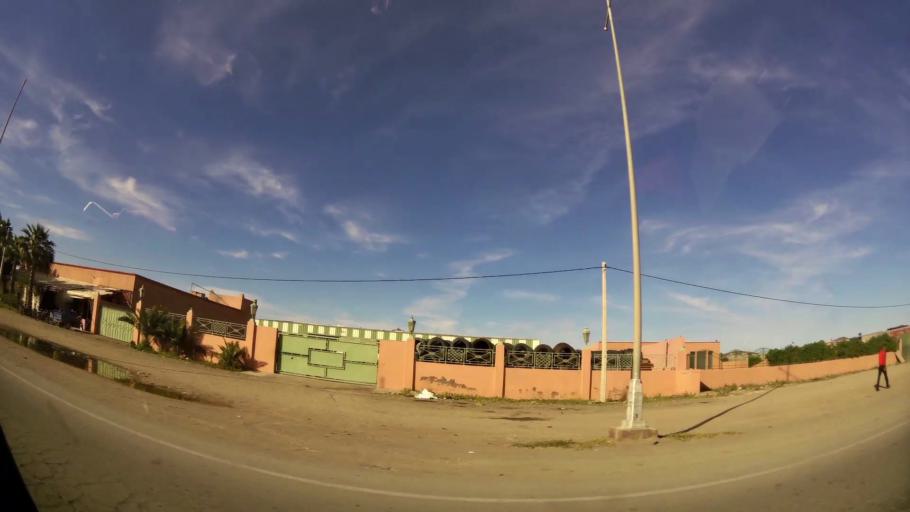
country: MA
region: Marrakech-Tensift-Al Haouz
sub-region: Marrakech
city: Marrakesh
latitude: 31.7161
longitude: -8.0774
